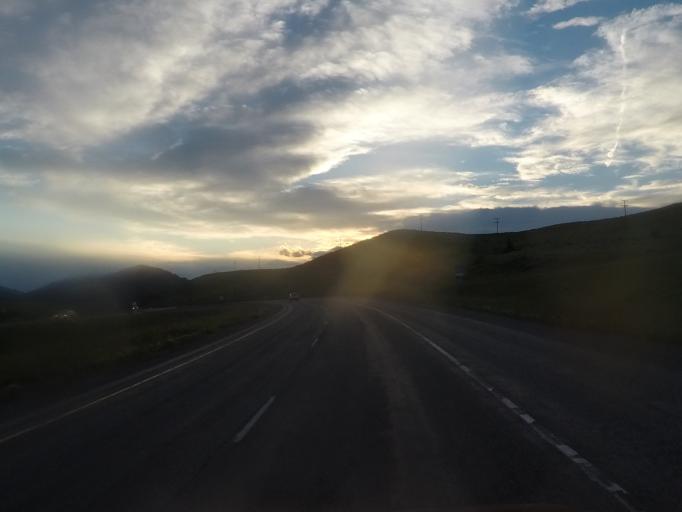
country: US
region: Montana
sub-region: Gallatin County
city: Bozeman
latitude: 45.6670
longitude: -110.8046
